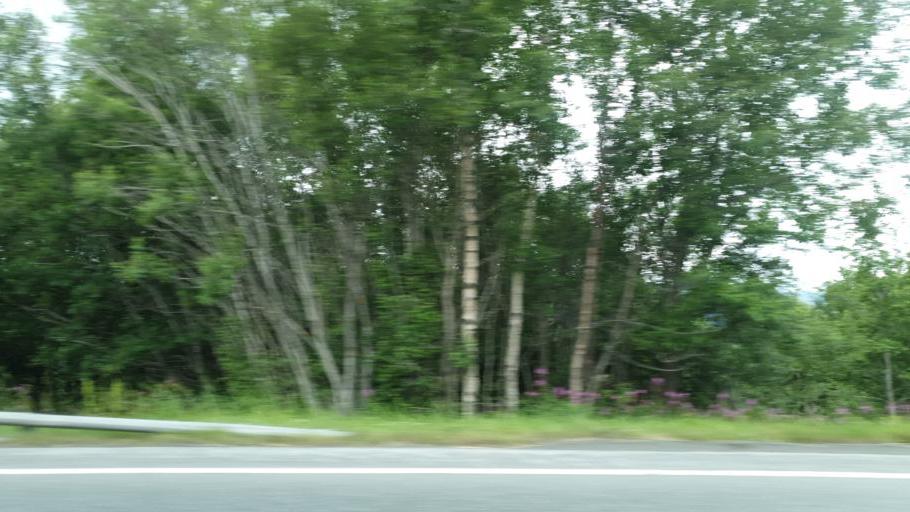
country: NO
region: Sor-Trondelag
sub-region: Rennebu
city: Berkak
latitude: 62.8254
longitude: 10.0083
